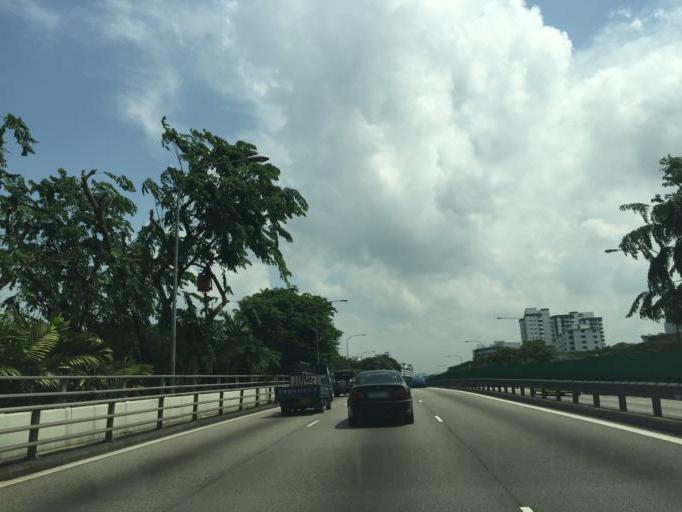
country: SG
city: Singapore
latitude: 1.3231
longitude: 103.8916
